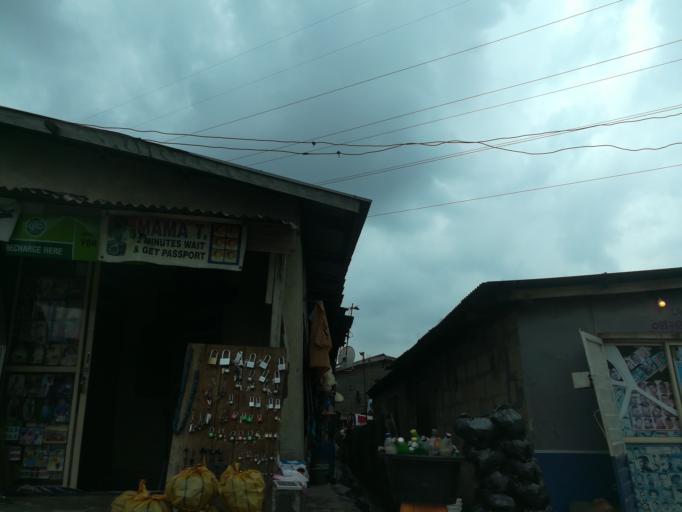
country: NG
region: Lagos
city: Ojota
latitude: 6.6086
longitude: 3.3991
